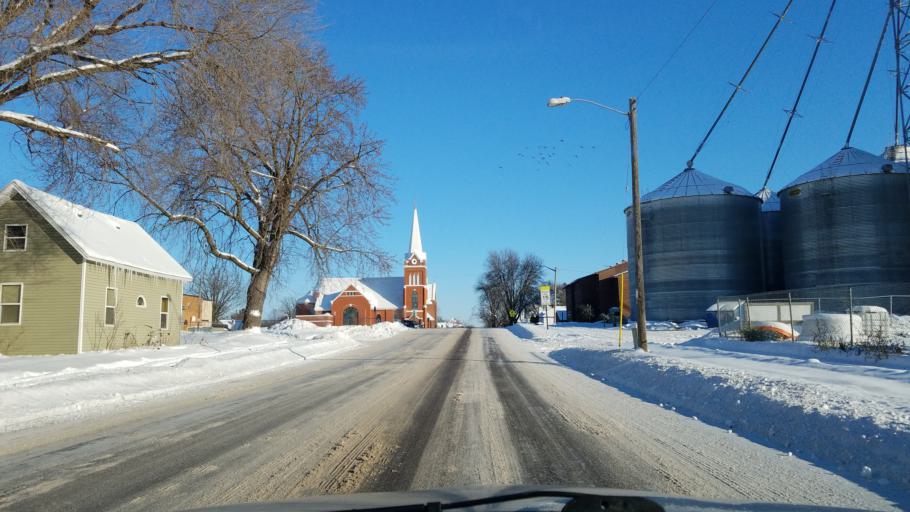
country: US
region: Wisconsin
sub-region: Barron County
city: Rice Lake
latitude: 45.5043
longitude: -91.7400
